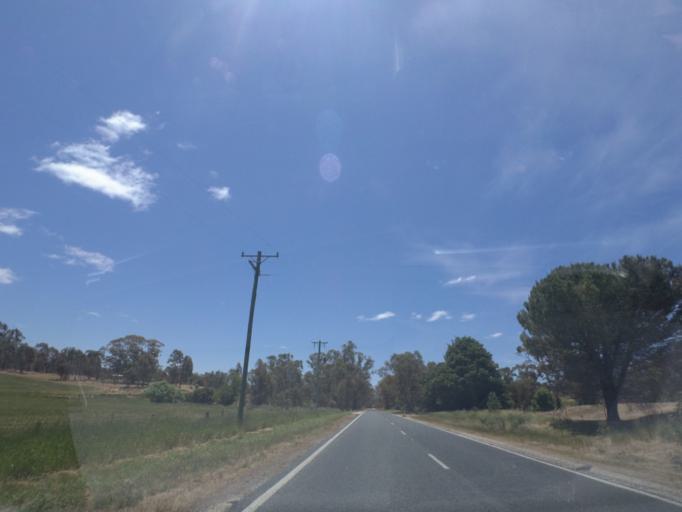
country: AU
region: Victoria
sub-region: Mount Alexander
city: Castlemaine
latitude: -37.1818
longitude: 144.1480
